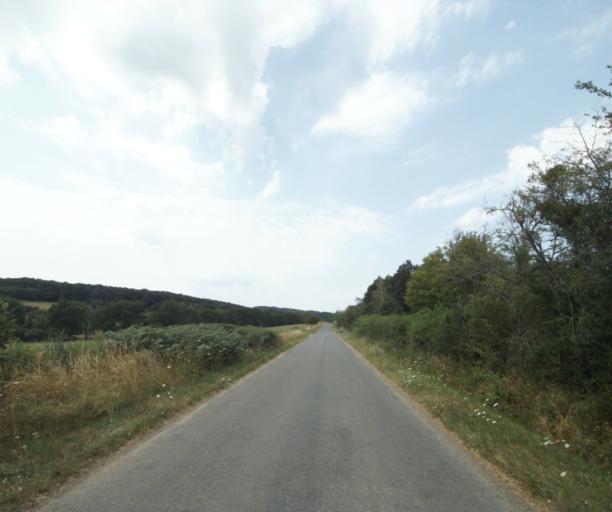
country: FR
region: Bourgogne
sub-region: Departement de Saone-et-Loire
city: Gueugnon
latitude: 46.5874
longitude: 4.0315
